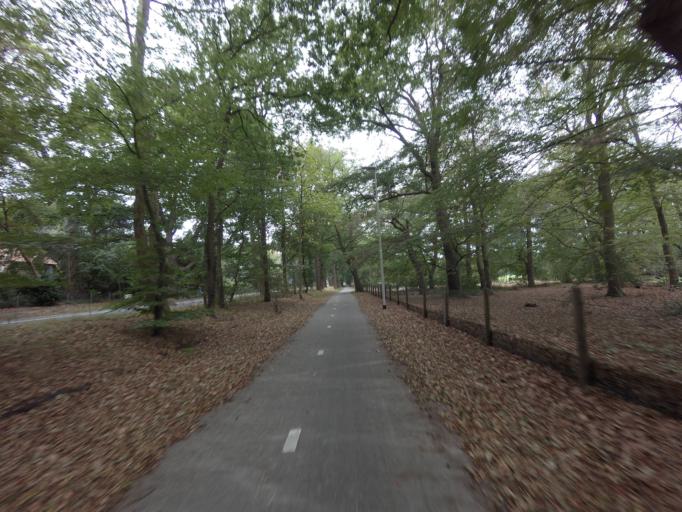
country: NL
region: North Holland
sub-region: Gemeente Wijdemeren
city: Nieuw-Loosdrecht
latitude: 52.1814
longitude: 5.1768
